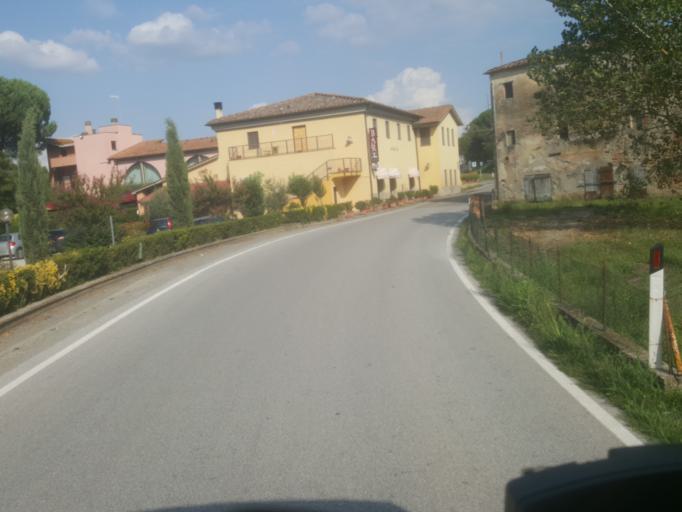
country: IT
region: Tuscany
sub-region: Province of Pisa
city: Volterra
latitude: 43.4542
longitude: 10.8271
